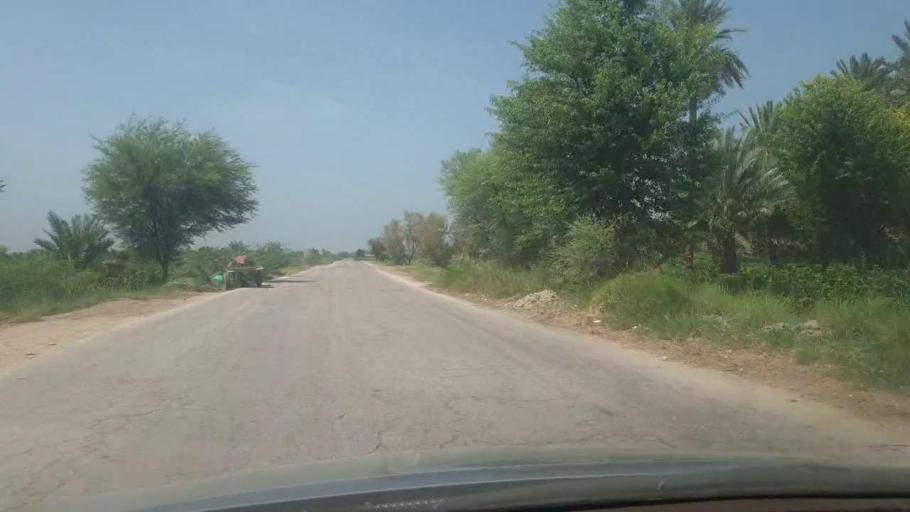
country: PK
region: Sindh
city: Ranipur
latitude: 27.2549
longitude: 68.5862
